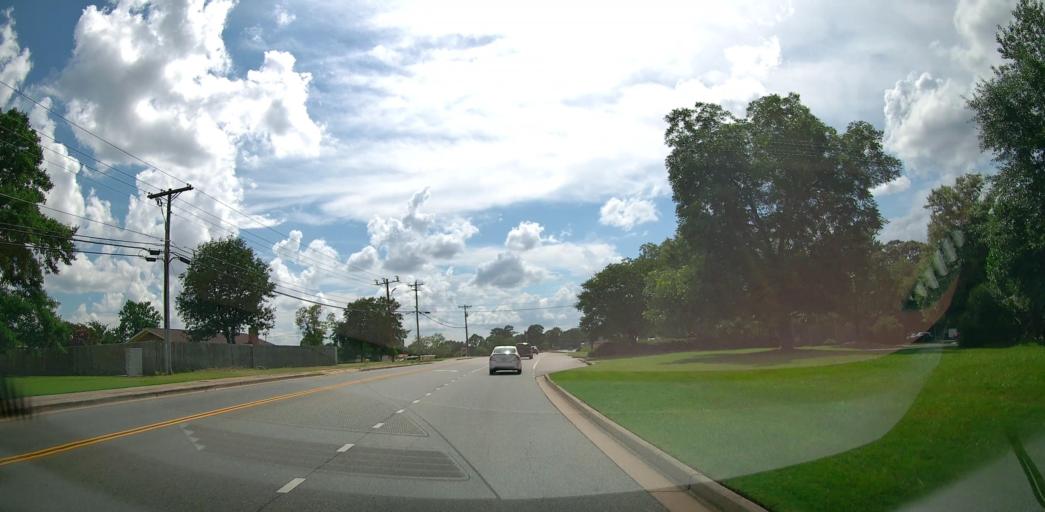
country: US
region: Georgia
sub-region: Houston County
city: Centerville
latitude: 32.6066
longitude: -83.6575
